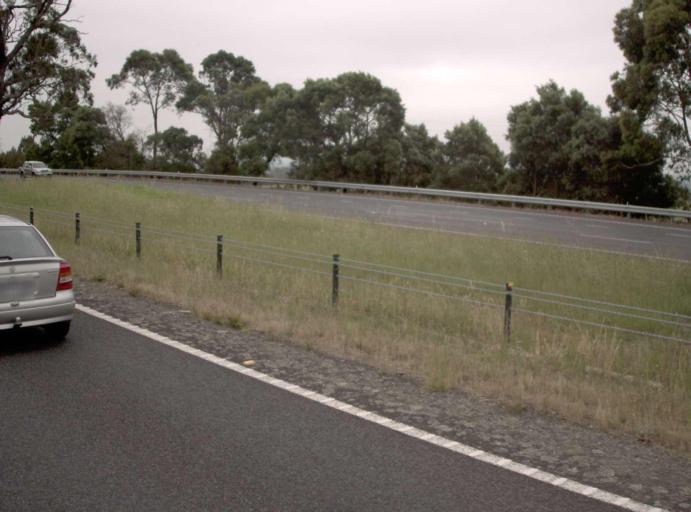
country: AU
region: Victoria
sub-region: Latrobe
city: Moe
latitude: -38.1947
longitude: 146.2056
